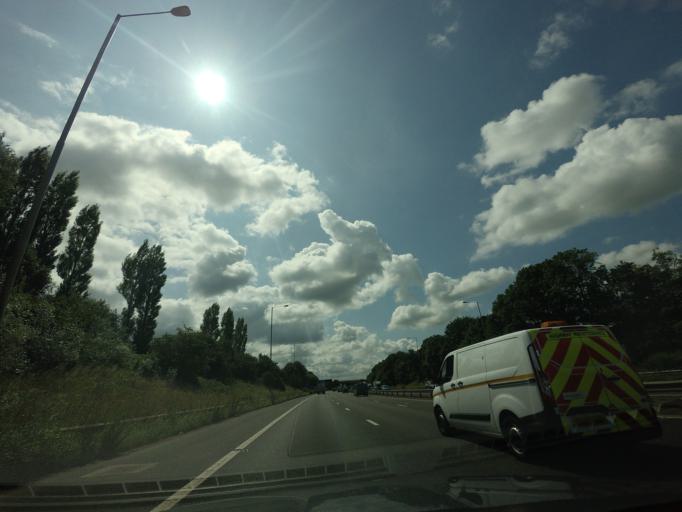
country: GB
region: England
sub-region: Lancashire
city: Clayton-le-Woods
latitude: 53.6902
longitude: -2.6776
